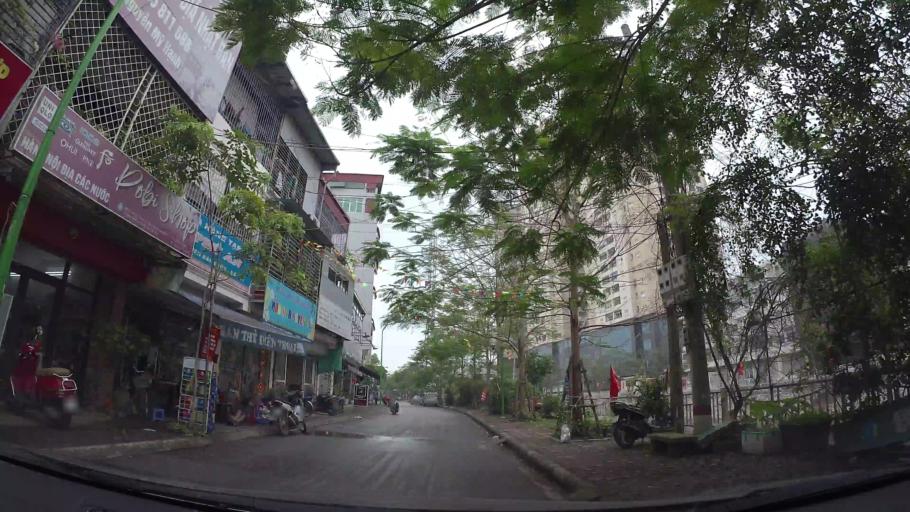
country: VN
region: Ha Noi
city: Hai BaTrung
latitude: 20.9809
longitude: 105.8460
